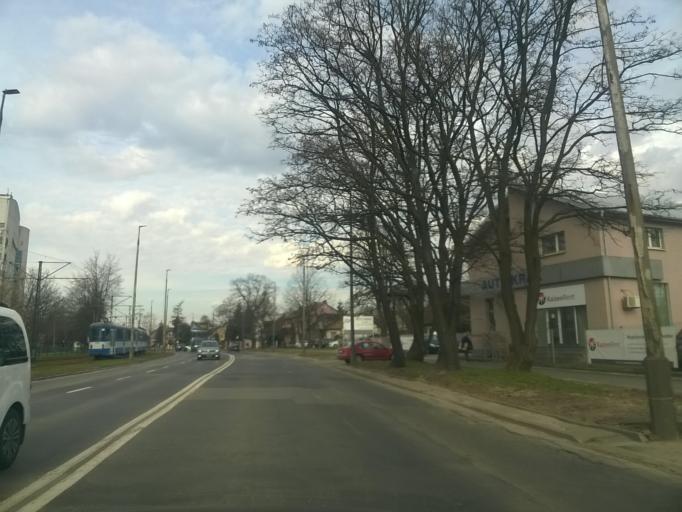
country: PL
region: Lesser Poland Voivodeship
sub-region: Powiat krakowski
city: Rzaska
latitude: 50.0820
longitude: 19.8875
